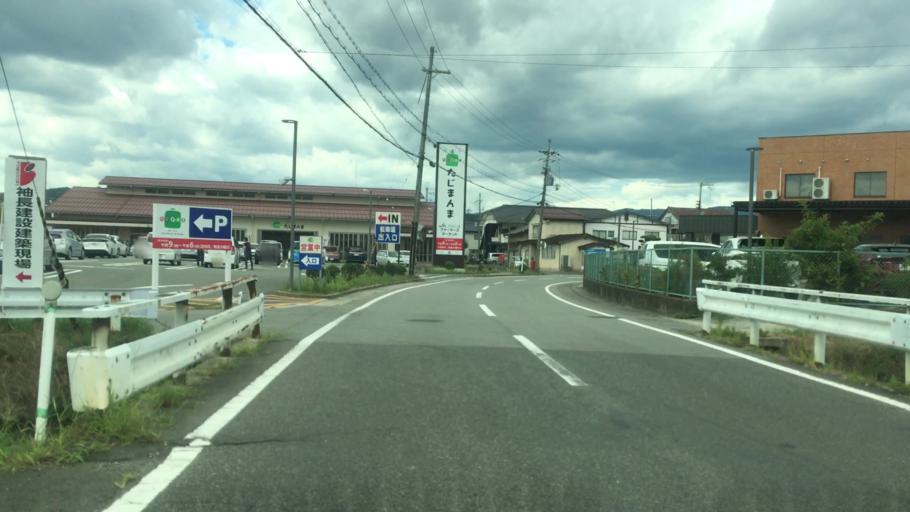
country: JP
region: Hyogo
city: Toyooka
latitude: 35.5246
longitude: 134.8354
